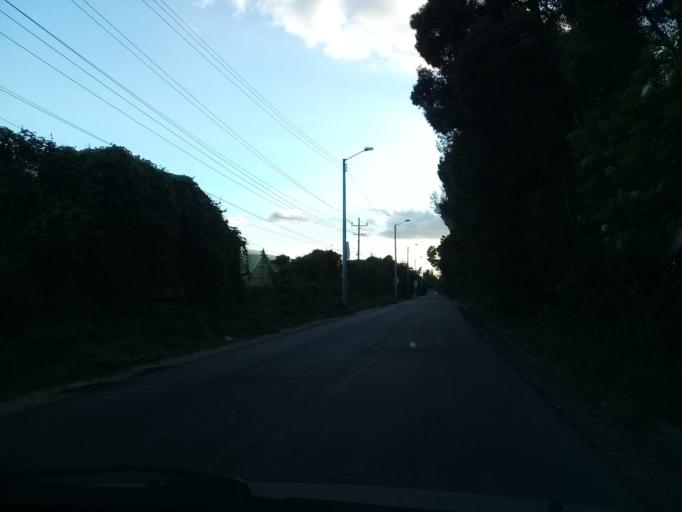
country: CO
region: Cundinamarca
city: Cota
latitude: 4.7902
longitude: -74.1535
